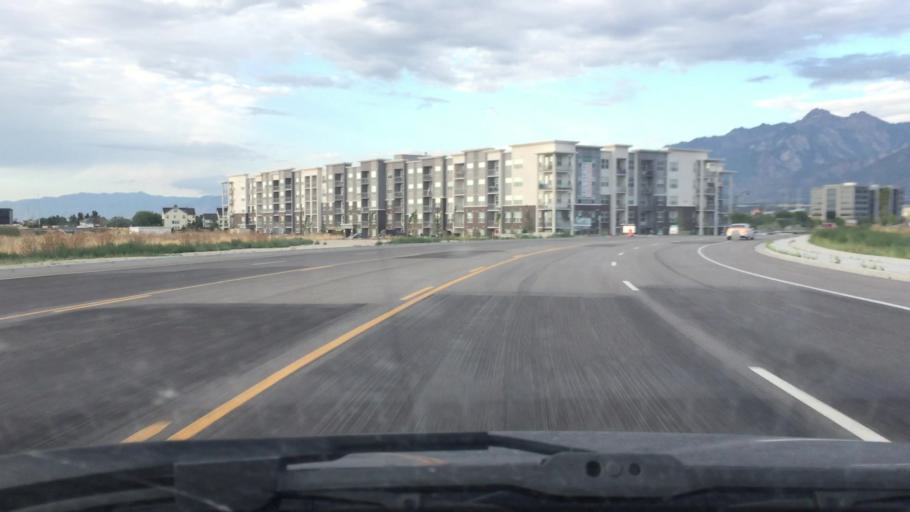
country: US
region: Utah
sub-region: Salt Lake County
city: Bluffdale
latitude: 40.5051
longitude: -111.9060
